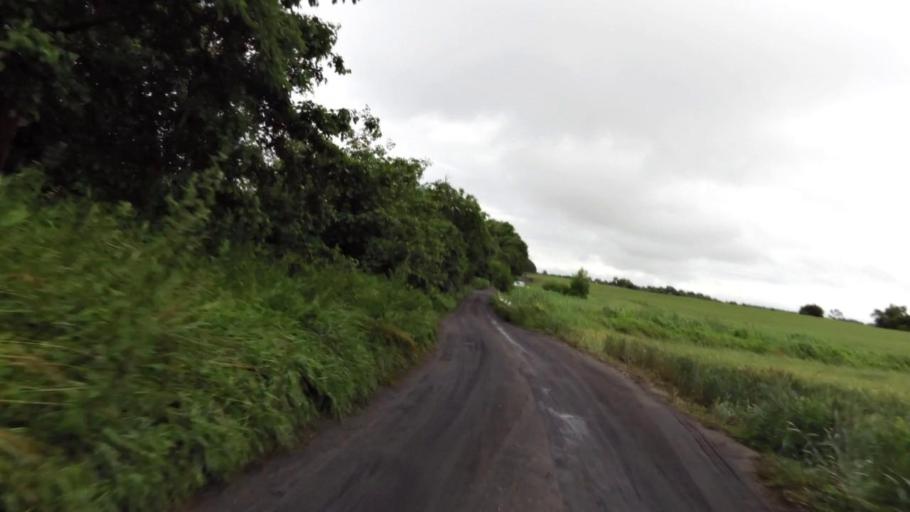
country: PL
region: West Pomeranian Voivodeship
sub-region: Powiat koszalinski
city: Mielno
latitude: 54.2462
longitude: 15.9152
